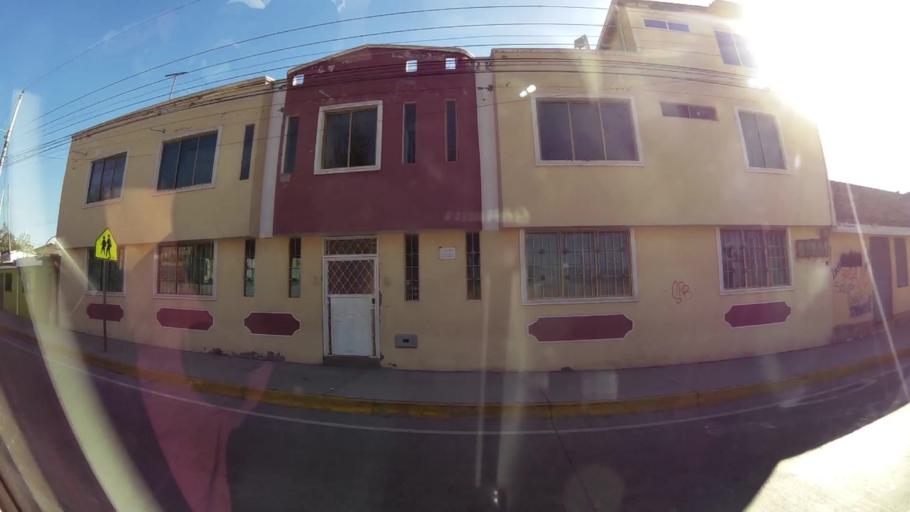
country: EC
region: Chimborazo
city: Riobamba
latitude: -1.6676
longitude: -78.6679
